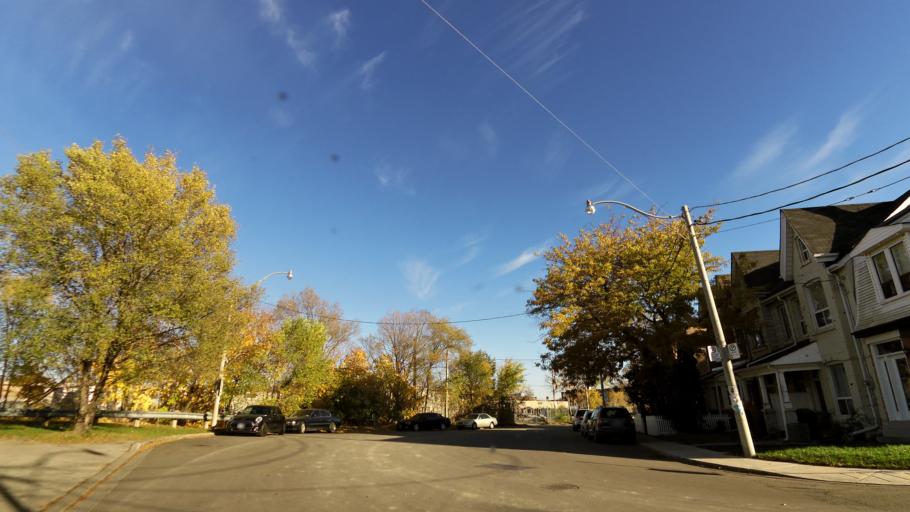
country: CA
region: Ontario
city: Toronto
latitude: 43.6657
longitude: -79.4600
